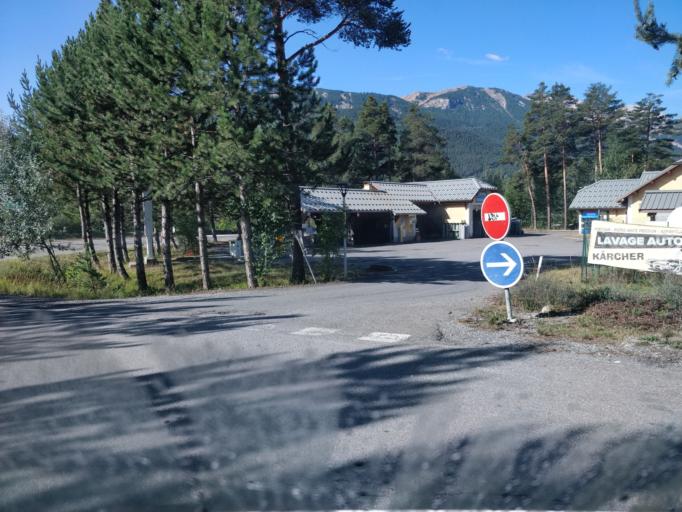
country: FR
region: Provence-Alpes-Cote d'Azur
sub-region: Departement des Alpes-de-Haute-Provence
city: Barcelonnette
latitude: 44.3869
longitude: 6.6293
